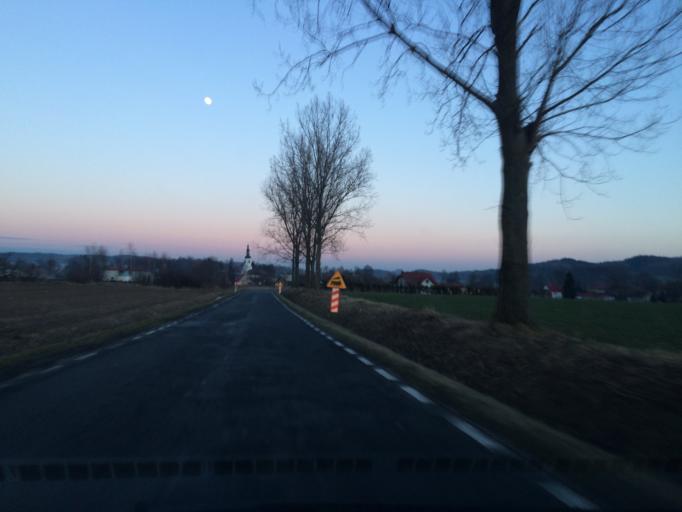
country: PL
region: Lower Silesian Voivodeship
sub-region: Powiat zlotoryjski
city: Olszanica
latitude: 51.1196
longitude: 15.8053
